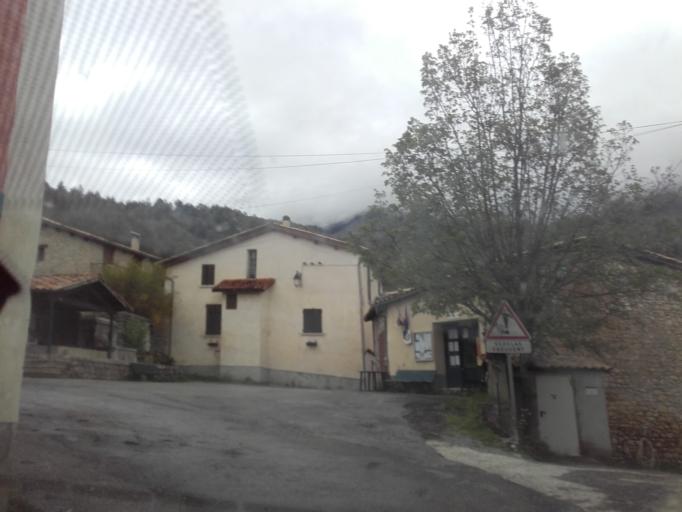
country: FR
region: Provence-Alpes-Cote d'Azur
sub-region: Departement des Alpes-de-Haute-Provence
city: Le Brusquet
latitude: 44.1214
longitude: 6.3339
